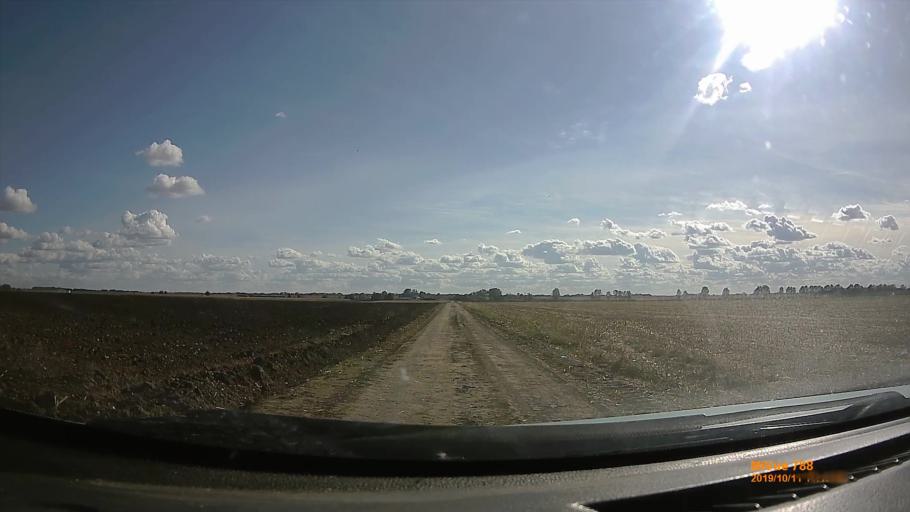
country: HU
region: Hajdu-Bihar
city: Hajduszoboszlo
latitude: 47.5381
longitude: 21.4012
